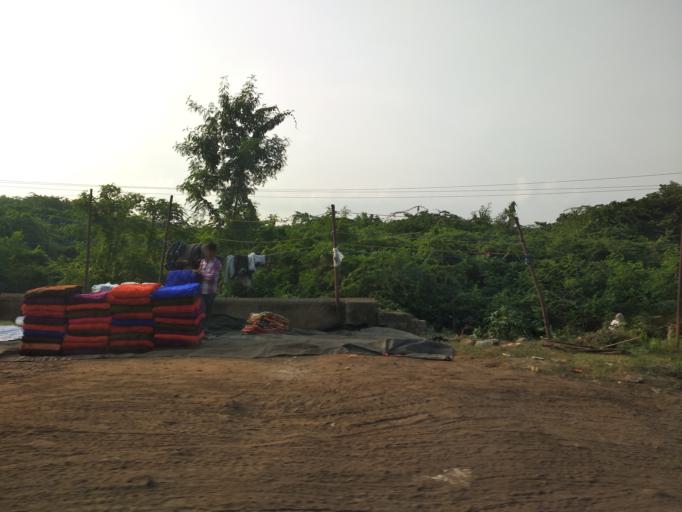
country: IN
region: Andhra Pradesh
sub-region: Vishakhapatnam
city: Visakhapatnam
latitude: 17.6847
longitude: 83.1642
